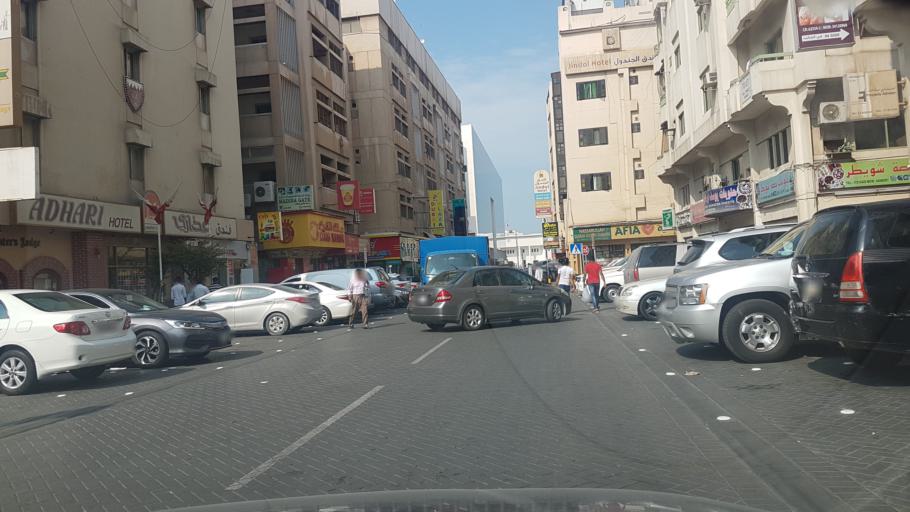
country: BH
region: Manama
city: Manama
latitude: 26.2312
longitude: 50.5741
